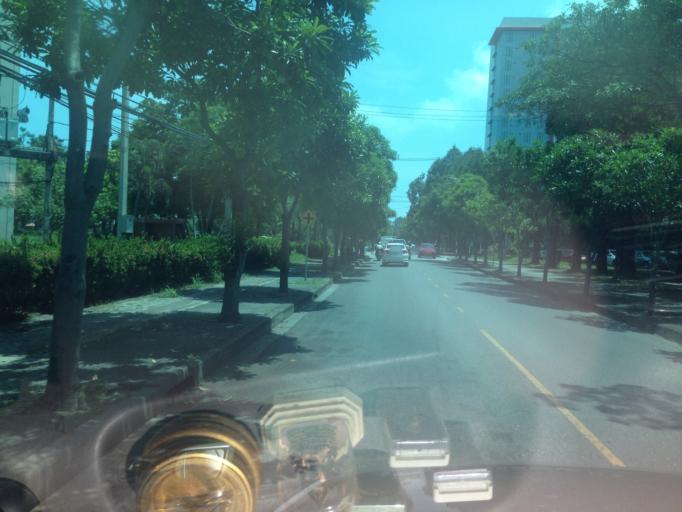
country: TH
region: Chon Buri
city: Si Racha
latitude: 13.2725
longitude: 100.9287
